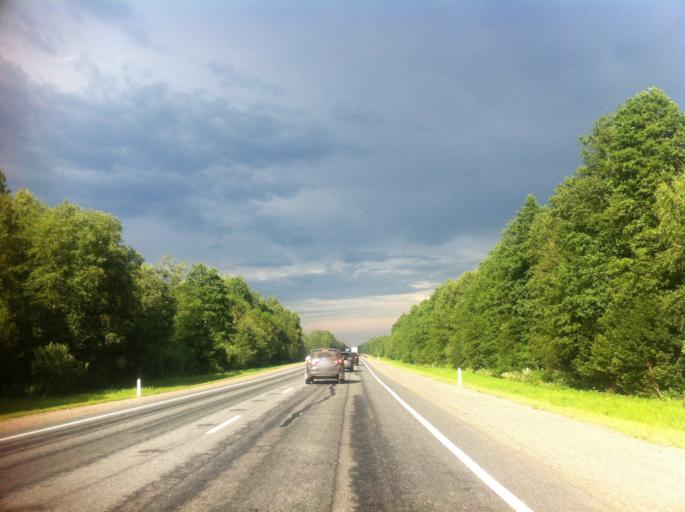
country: RU
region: Pskov
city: Plyussa
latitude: 58.2336
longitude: 29.3767
